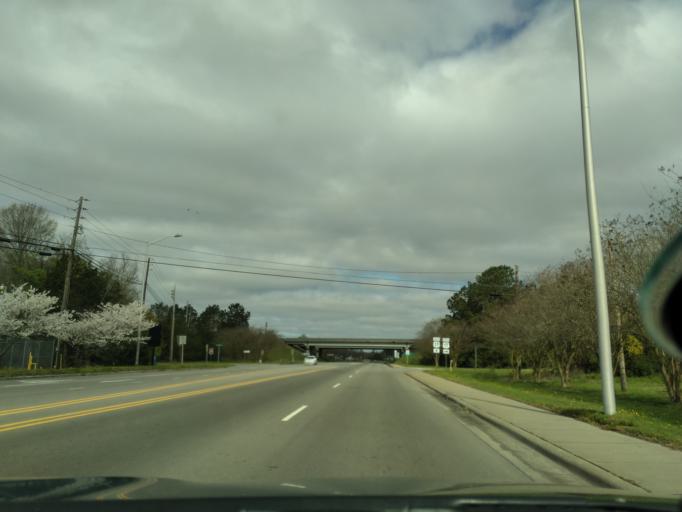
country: US
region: North Carolina
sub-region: Chowan County
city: Edenton
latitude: 36.0735
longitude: -76.6123
